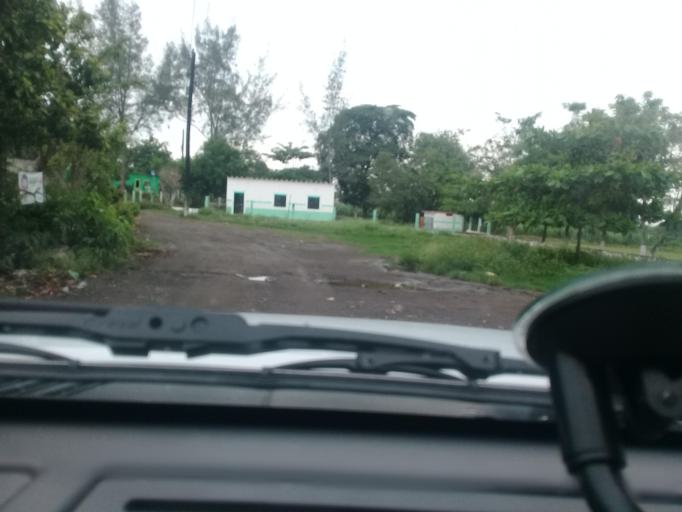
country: MX
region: Veracruz
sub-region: Puente Nacional
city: Chichicaxtle
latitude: 19.3679
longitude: -96.4329
